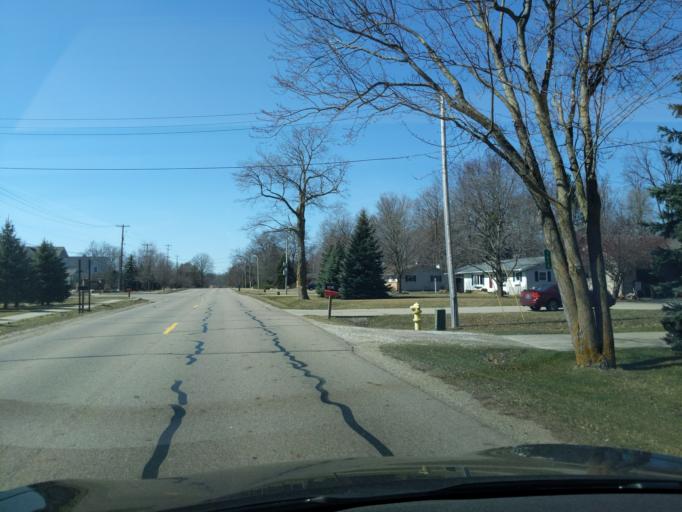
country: US
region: Michigan
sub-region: Eaton County
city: Grand Ledge
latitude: 42.7266
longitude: -84.6931
